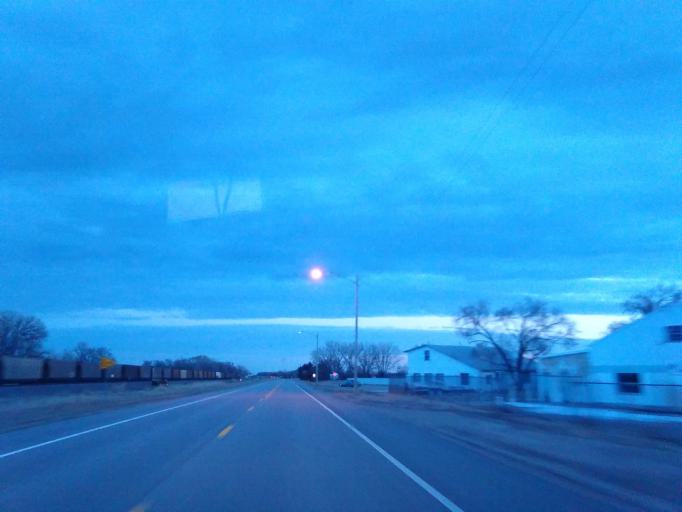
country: US
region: Nebraska
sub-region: Garden County
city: Oshkosh
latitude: 41.3300
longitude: -102.1376
